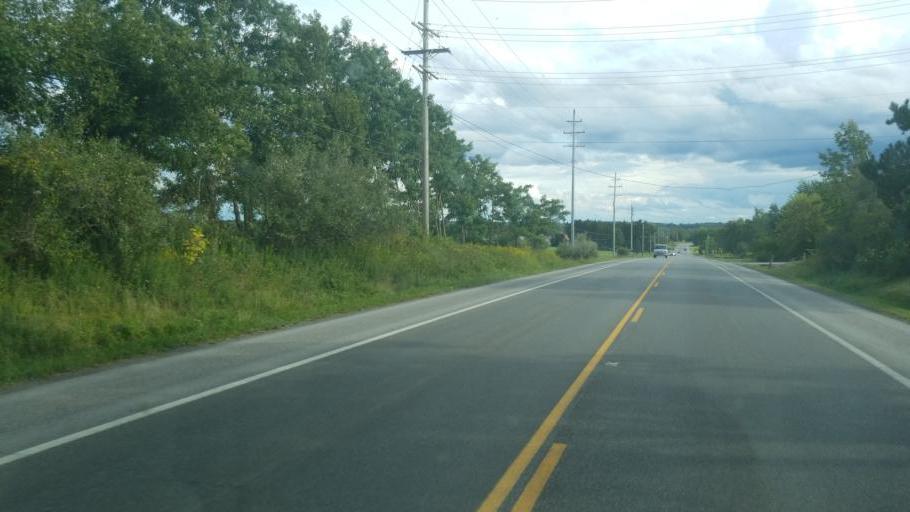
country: US
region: Ohio
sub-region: Geauga County
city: Middlefield
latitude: 41.4540
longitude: -81.0513
